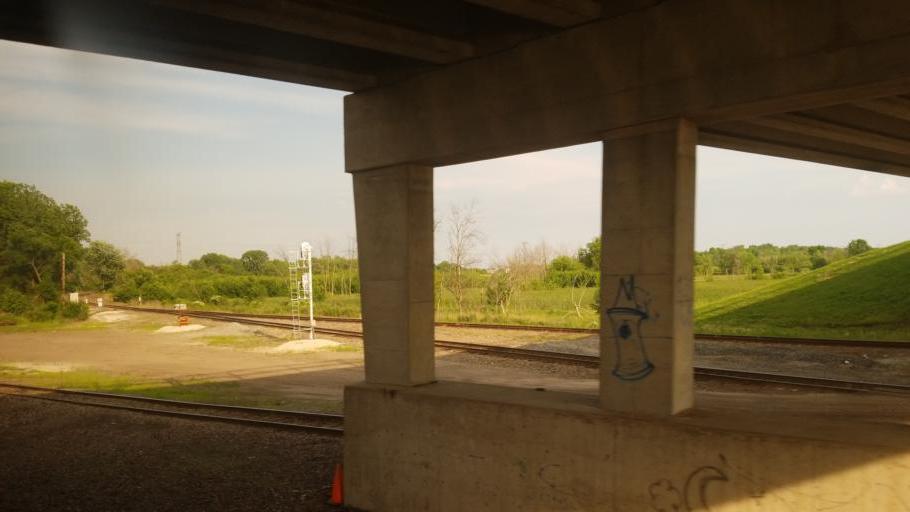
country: US
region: Illinois
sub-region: DuPage County
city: Warrenville
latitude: 41.7752
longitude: -88.2411
